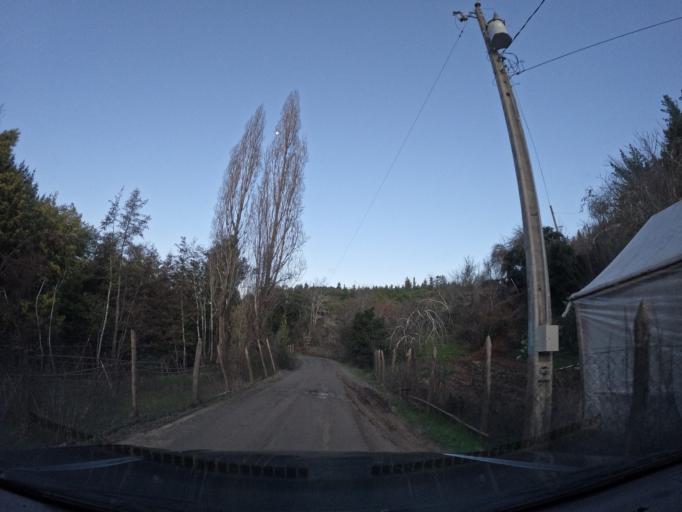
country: CL
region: Biobio
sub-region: Provincia de Concepcion
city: Chiguayante
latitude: -36.9943
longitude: -72.8287
